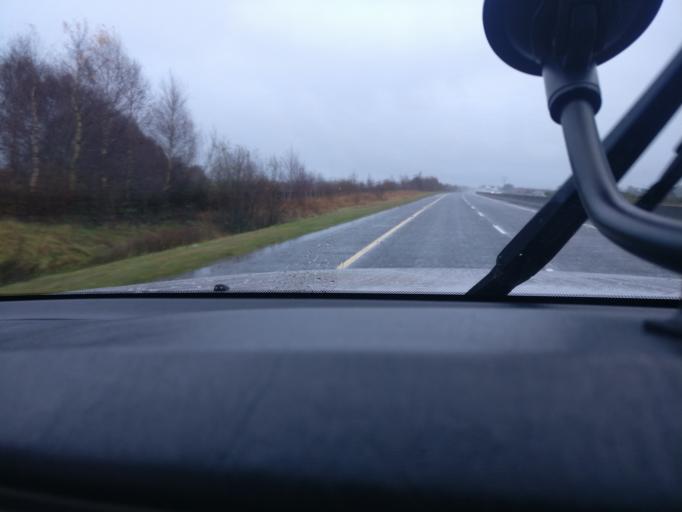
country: IE
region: Leinster
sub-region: An Iarmhi
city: Rochfortbridge
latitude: 53.4411
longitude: -7.2072
